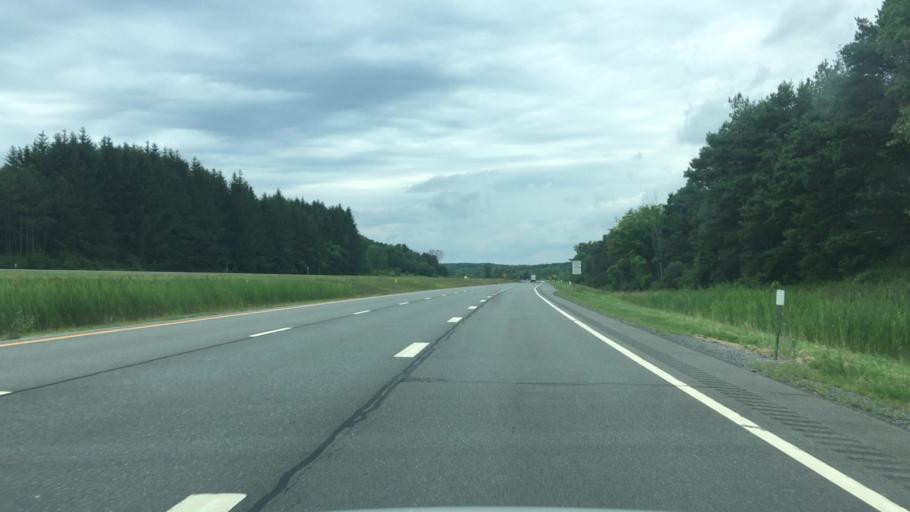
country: US
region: New York
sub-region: Schoharie County
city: Schoharie
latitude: 42.7241
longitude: -74.2296
